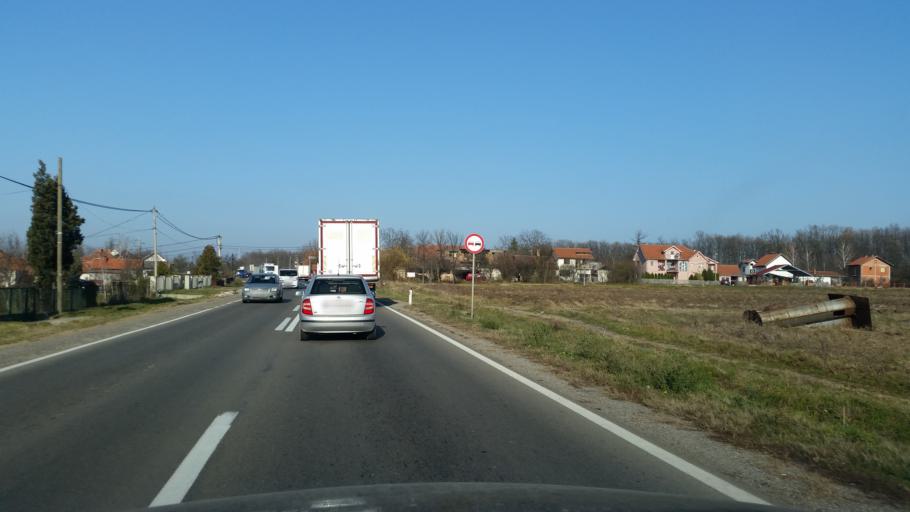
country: RS
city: Stepojevac
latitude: 44.5431
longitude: 20.3005
